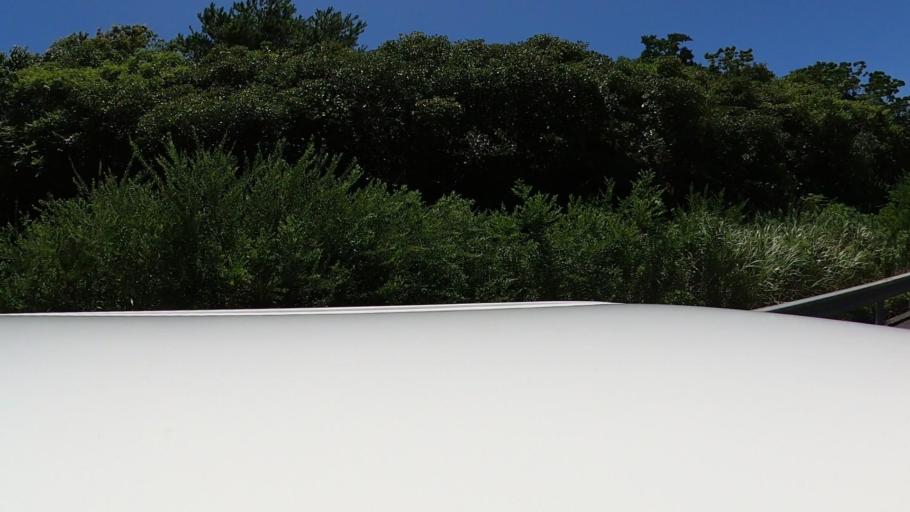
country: JP
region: Miyazaki
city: Nobeoka
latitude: 32.5381
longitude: 131.6593
